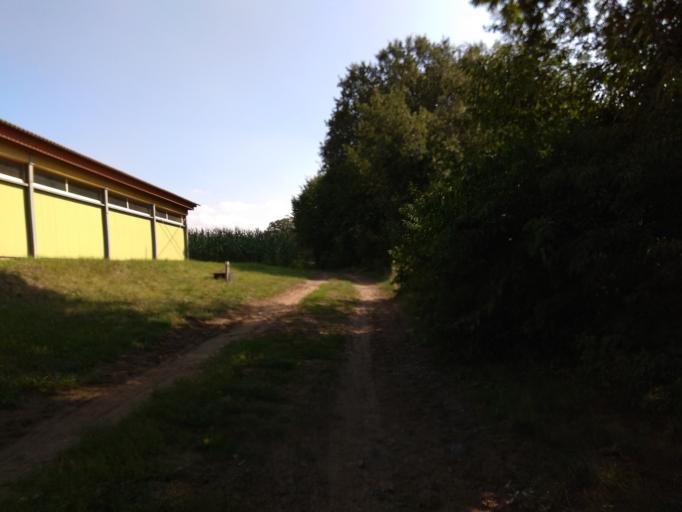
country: DE
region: North Rhine-Westphalia
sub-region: Regierungsbezirk Munster
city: Klein Reken
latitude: 51.7476
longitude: 7.0358
